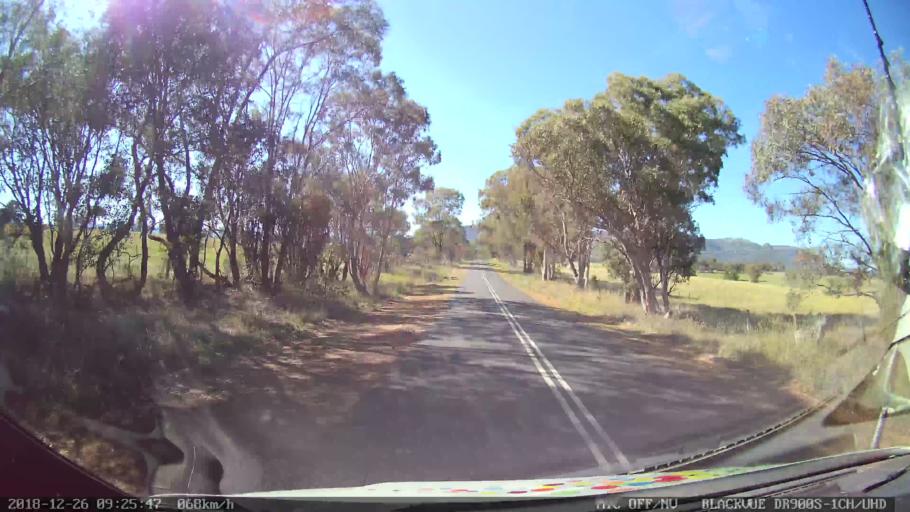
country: AU
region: New South Wales
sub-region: Mid-Western Regional
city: Kandos
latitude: -32.8232
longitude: 150.0052
